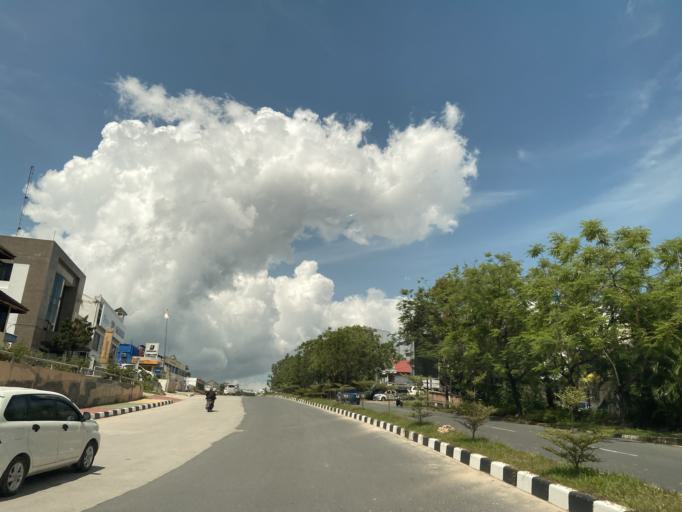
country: SG
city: Singapore
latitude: 1.1397
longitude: 104.0158
